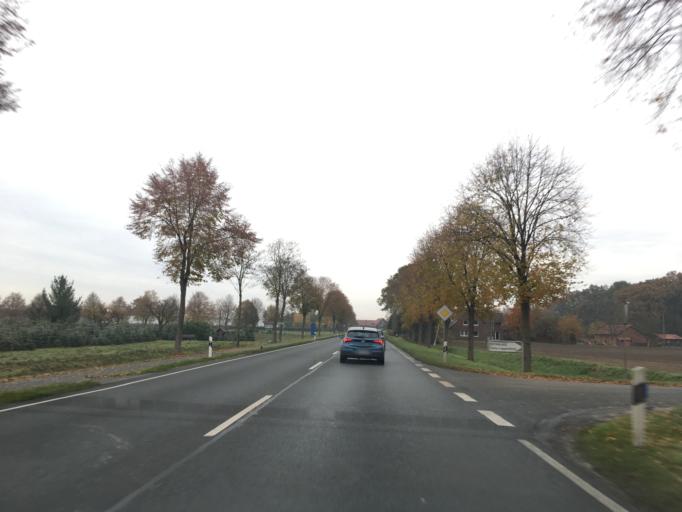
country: DE
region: North Rhine-Westphalia
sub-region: Regierungsbezirk Munster
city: Telgte
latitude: 51.9921
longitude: 7.8028
